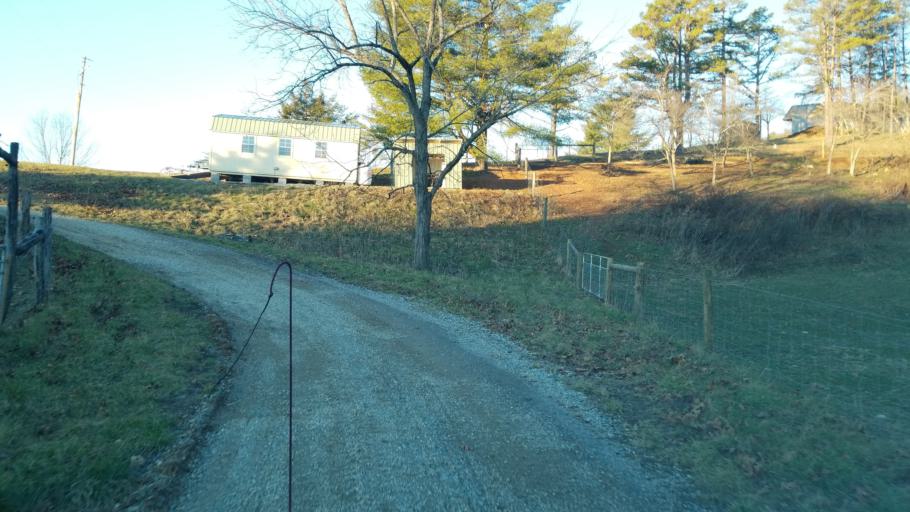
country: US
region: Virginia
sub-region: Giles County
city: Narrows
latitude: 37.1933
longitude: -80.8467
